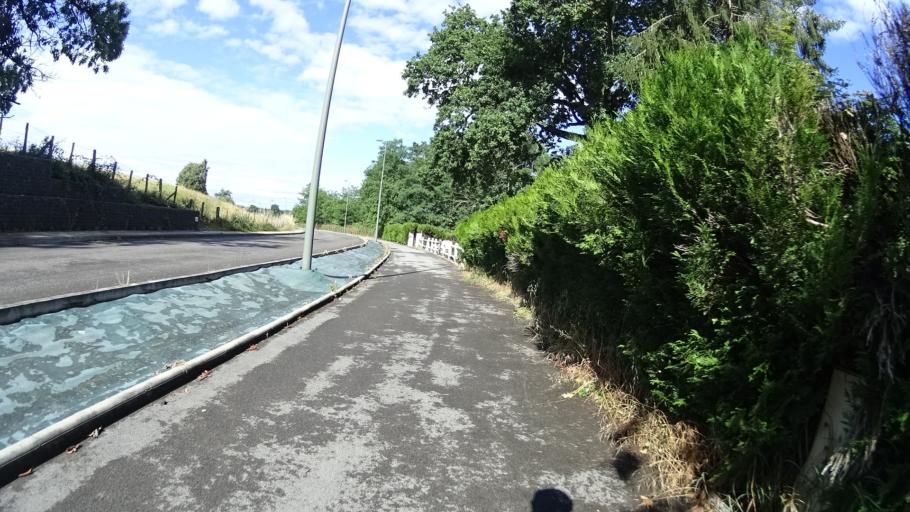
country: FR
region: Aquitaine
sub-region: Departement des Landes
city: Dax
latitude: 43.6978
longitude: -1.0751
